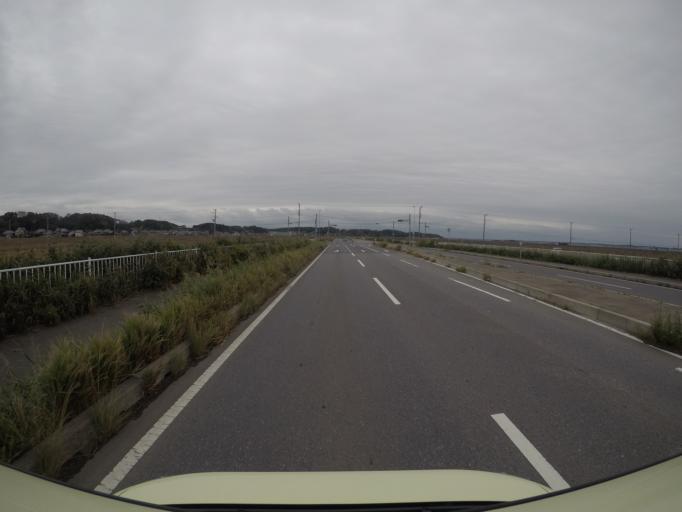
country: JP
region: Ibaraki
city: Ami
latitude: 36.0932
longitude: 140.2306
